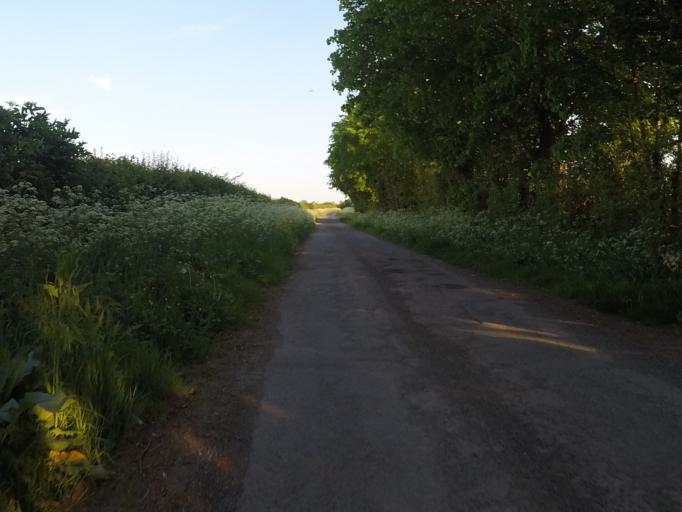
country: GB
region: England
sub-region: Oxfordshire
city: Shipton under Wychwood
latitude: 51.8596
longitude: -1.5544
